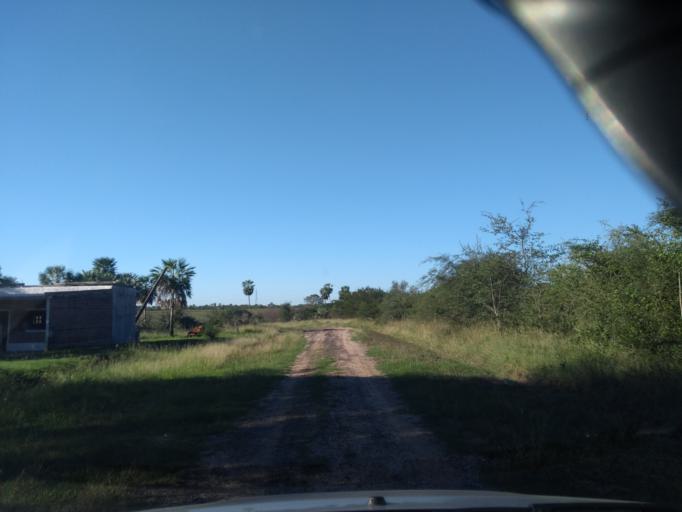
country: AR
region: Chaco
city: Barranqueras
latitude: -27.4402
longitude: -58.9030
